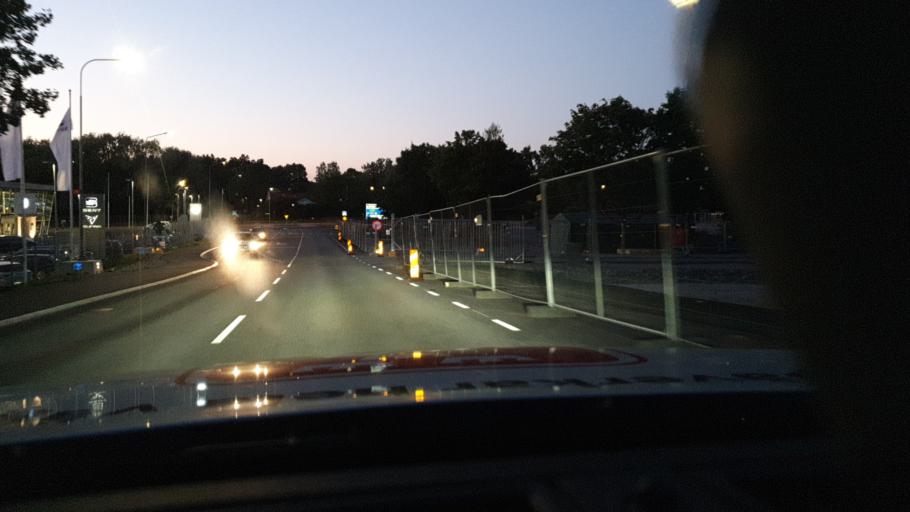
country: SE
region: Stockholm
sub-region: Taby Kommun
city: Taby
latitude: 59.4369
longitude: 18.0541
